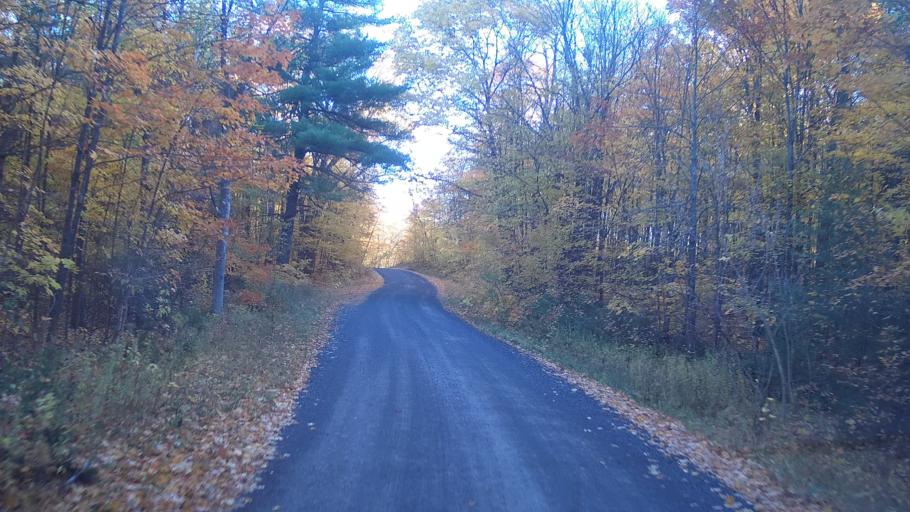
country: CA
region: Ontario
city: Arnprior
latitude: 45.3396
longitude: -76.3511
